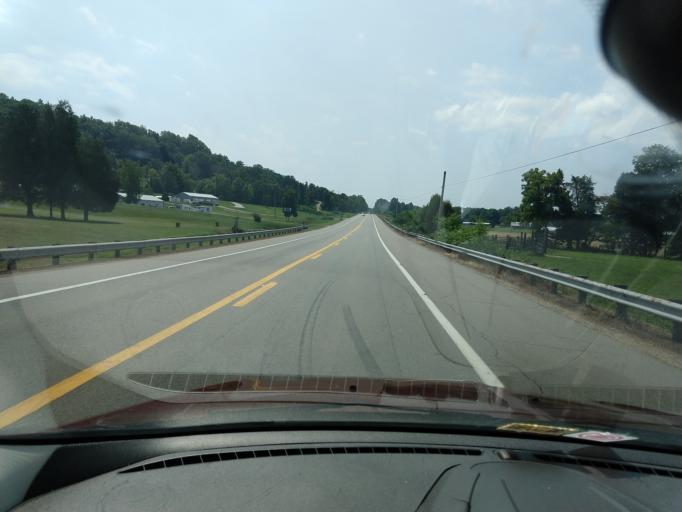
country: US
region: West Virginia
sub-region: Jackson County
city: Ripley
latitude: 38.8567
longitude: -81.8032
